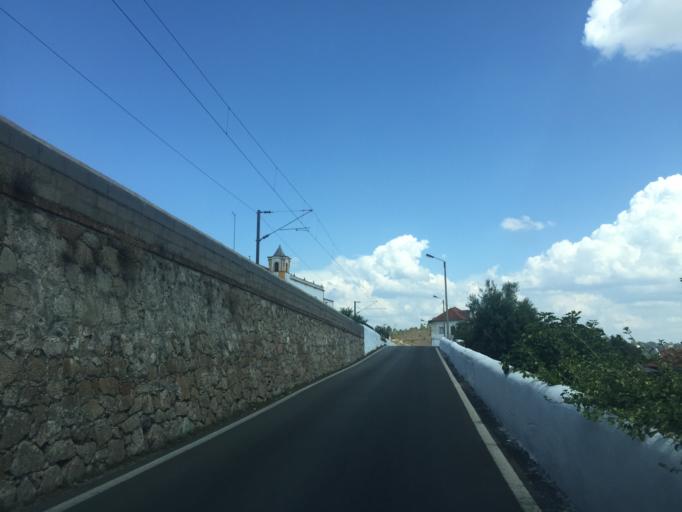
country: PT
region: Santarem
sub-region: Chamusca
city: Vila Nova da Barquinha
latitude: 39.4588
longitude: -8.4006
